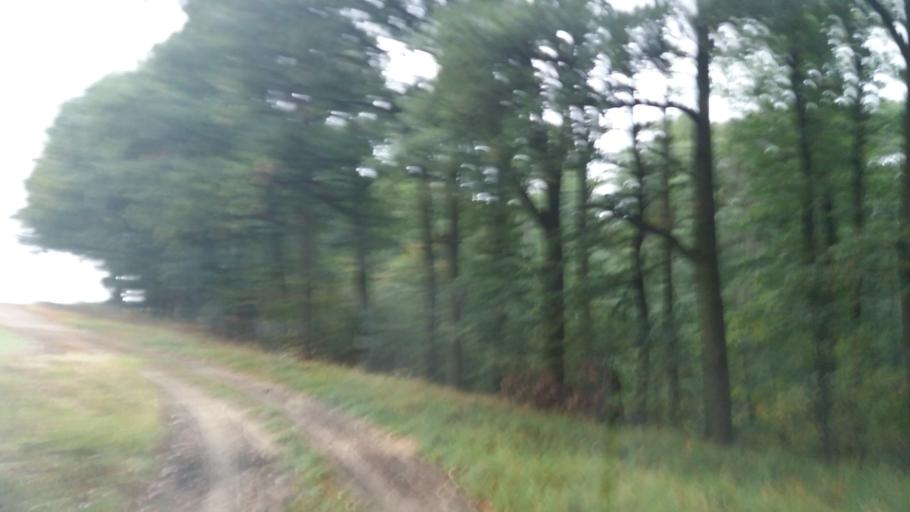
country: PL
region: West Pomeranian Voivodeship
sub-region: Powiat choszczenski
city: Pelczyce
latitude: 53.0701
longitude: 15.2742
